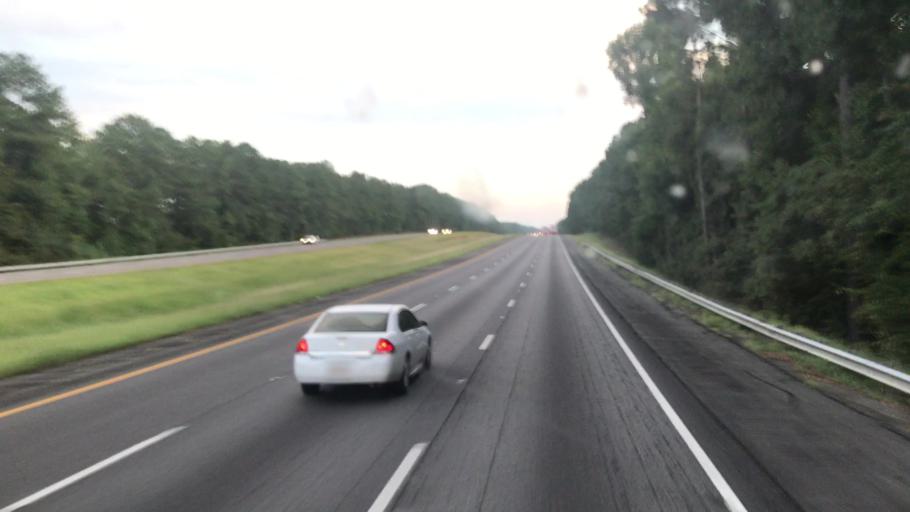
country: US
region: Georgia
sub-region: Dooly County
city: Unadilla
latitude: 32.3551
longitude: -83.7682
